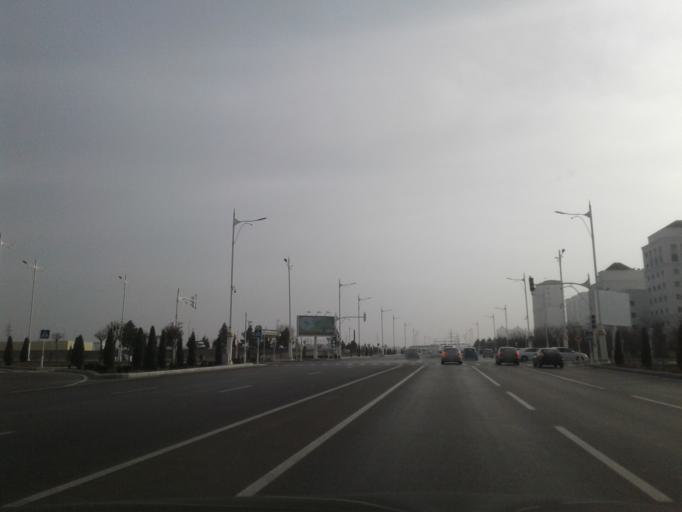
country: TM
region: Ahal
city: Ashgabat
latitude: 37.8998
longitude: 58.3978
